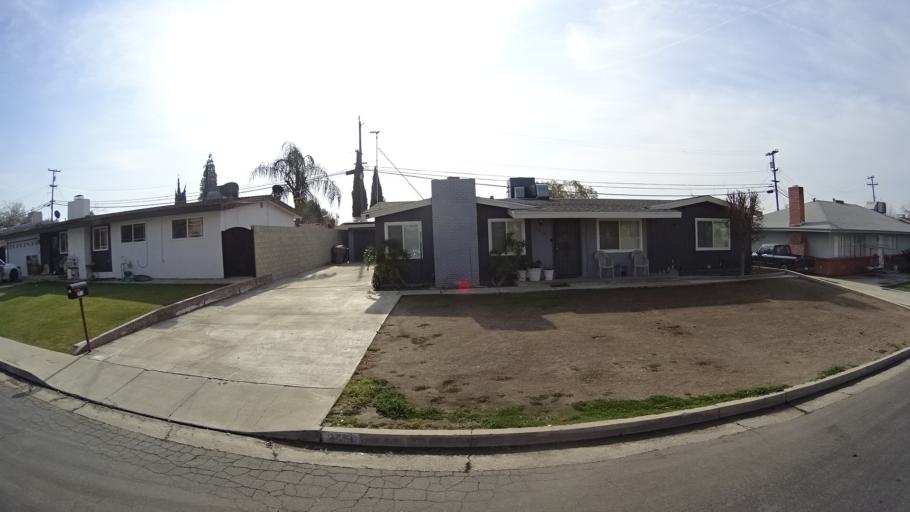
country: US
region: California
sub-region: Kern County
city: Oildale
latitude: 35.4042
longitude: -118.9657
